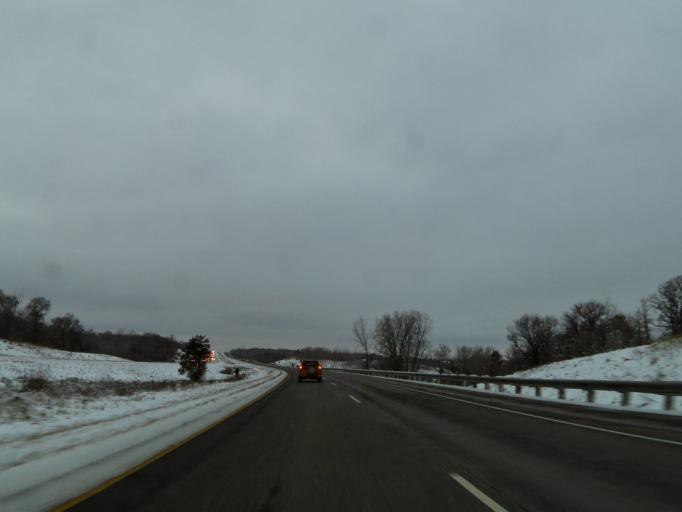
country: US
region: Wisconsin
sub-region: Saint Croix County
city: Roberts
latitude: 44.9631
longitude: -92.6197
